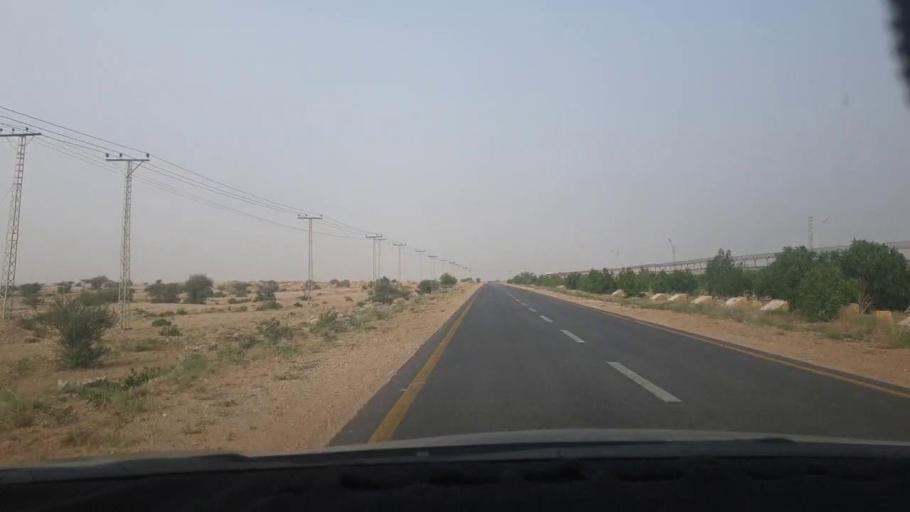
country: PK
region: Sindh
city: Jamshoro
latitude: 25.5467
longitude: 68.3201
